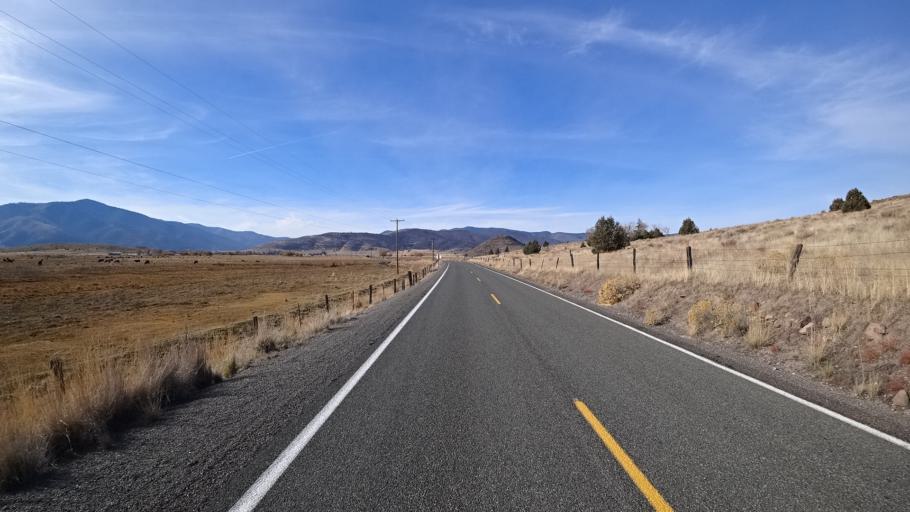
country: US
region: California
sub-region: Siskiyou County
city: Weed
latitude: 41.5373
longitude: -122.5054
